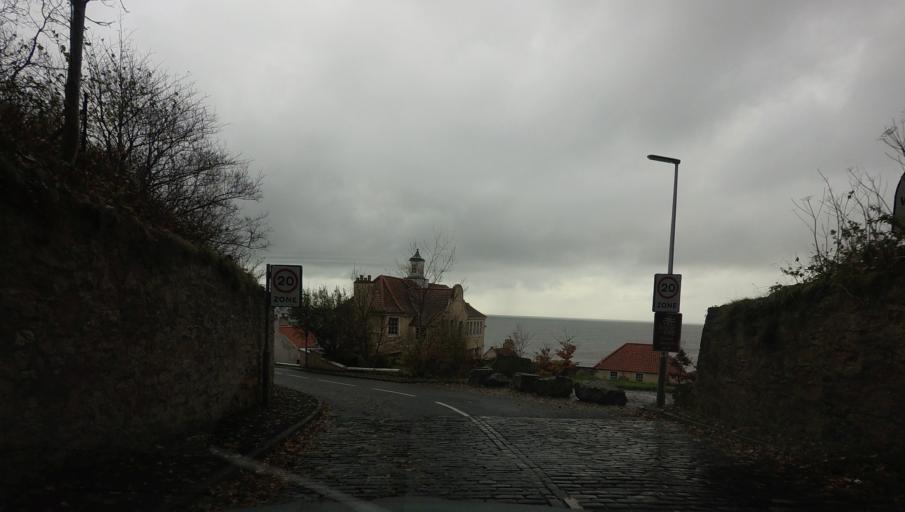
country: GB
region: Scotland
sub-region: Fife
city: East Wemyss
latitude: 56.1404
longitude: -3.0886
